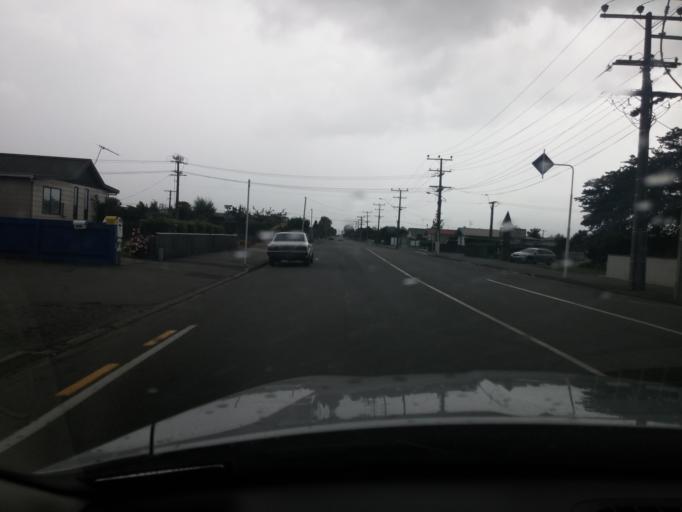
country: NZ
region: Marlborough
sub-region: Marlborough District
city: Blenheim
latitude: -41.5078
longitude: 173.9557
